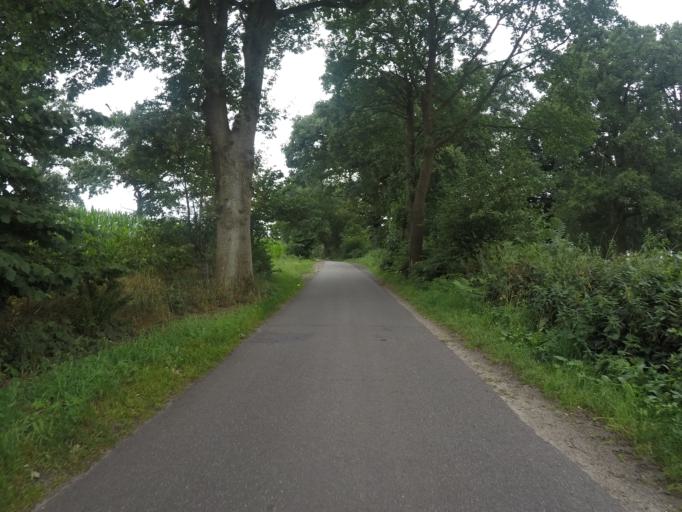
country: DE
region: Lower Saxony
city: Himmelpforten
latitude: 53.6074
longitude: 9.3310
